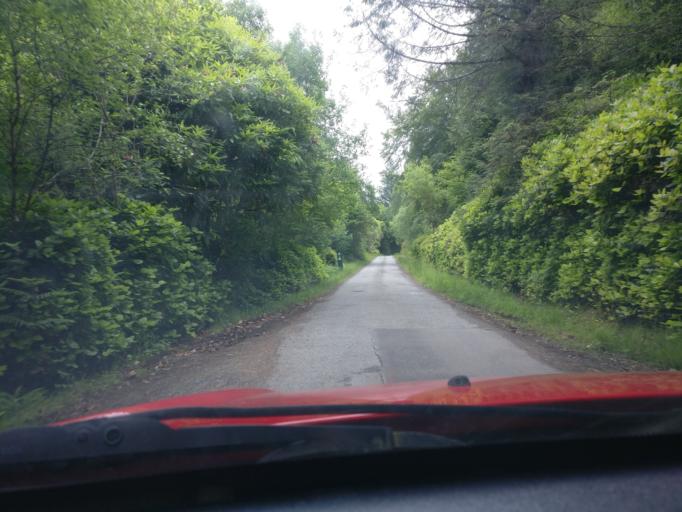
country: GB
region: Scotland
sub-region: Argyll and Bute
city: Isle Of Mull
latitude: 56.6097
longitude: -6.0492
